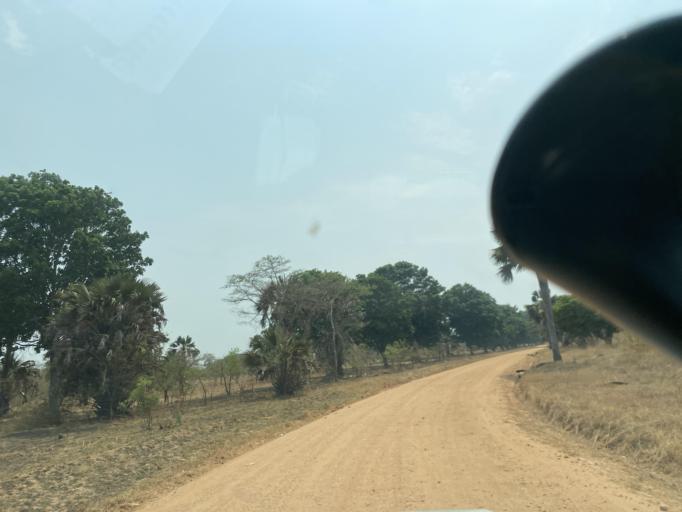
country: ZM
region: Lusaka
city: Kafue
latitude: -15.6242
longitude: 28.0973
